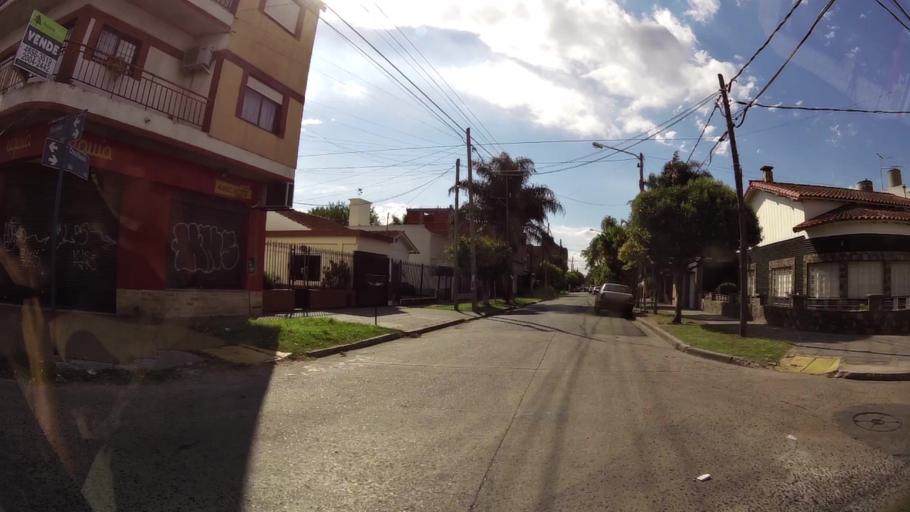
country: AR
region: Buenos Aires
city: San Justo
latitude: -34.6533
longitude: -58.5774
